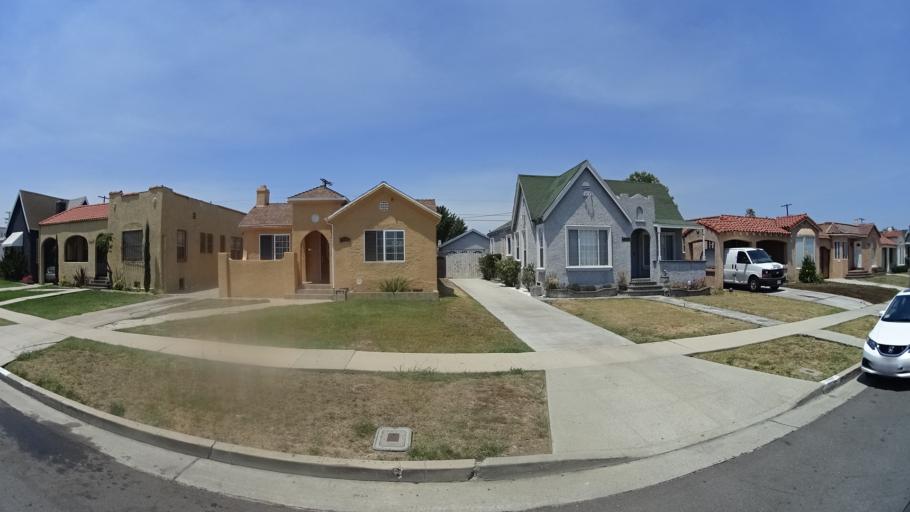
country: US
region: California
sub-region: Los Angeles County
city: Westmont
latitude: 33.9718
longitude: -118.3071
